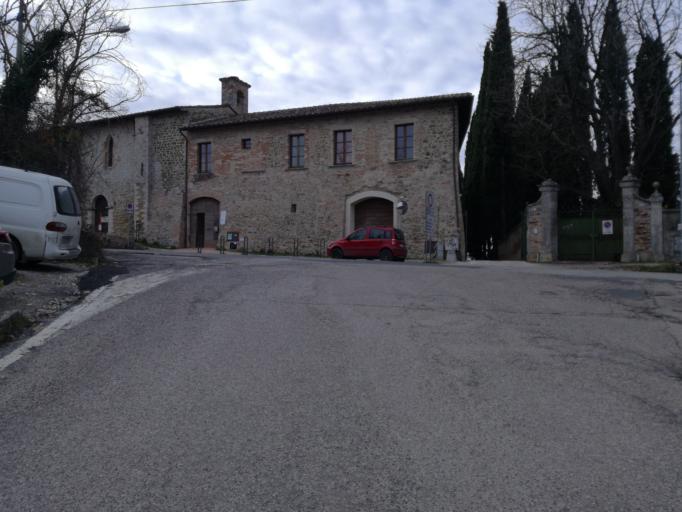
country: IT
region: Umbria
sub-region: Provincia di Perugia
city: Perugia
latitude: 43.1205
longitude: 12.3833
